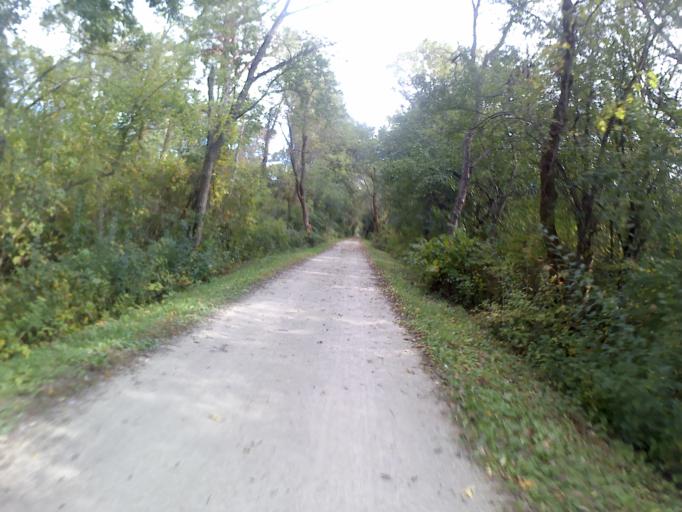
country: US
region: Illinois
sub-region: DuPage County
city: West Chicago
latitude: 41.8979
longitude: -88.1704
